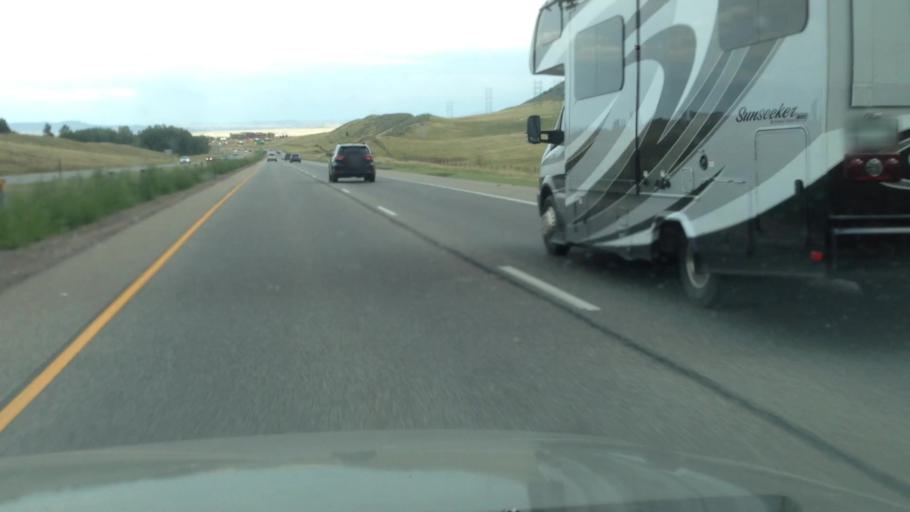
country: US
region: Colorado
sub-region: Jefferson County
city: Ken Caryl
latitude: 39.5711
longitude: -105.1359
